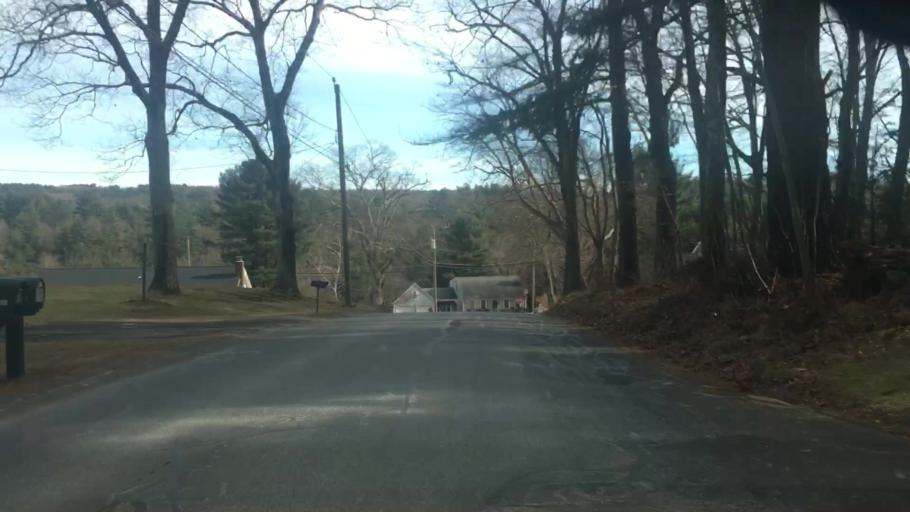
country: US
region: Connecticut
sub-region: Tolland County
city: Stafford
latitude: 41.9750
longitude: -72.2983
